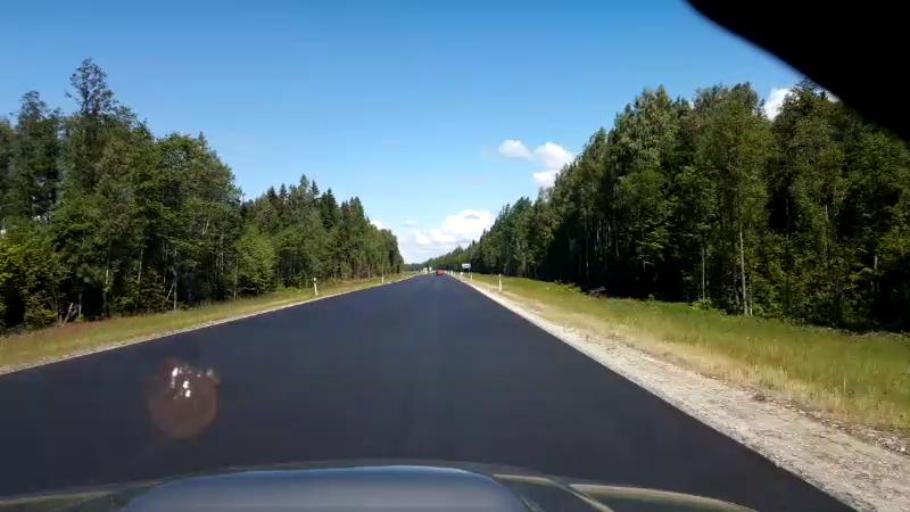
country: LV
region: Salacgrivas
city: Ainazi
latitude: 58.0368
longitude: 24.5069
